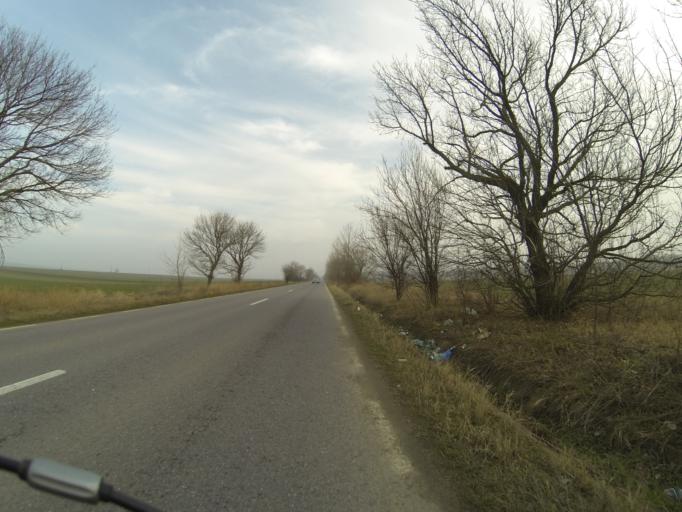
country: RO
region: Mehedinti
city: Vanju-Mare
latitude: 44.4068
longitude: 22.8925
